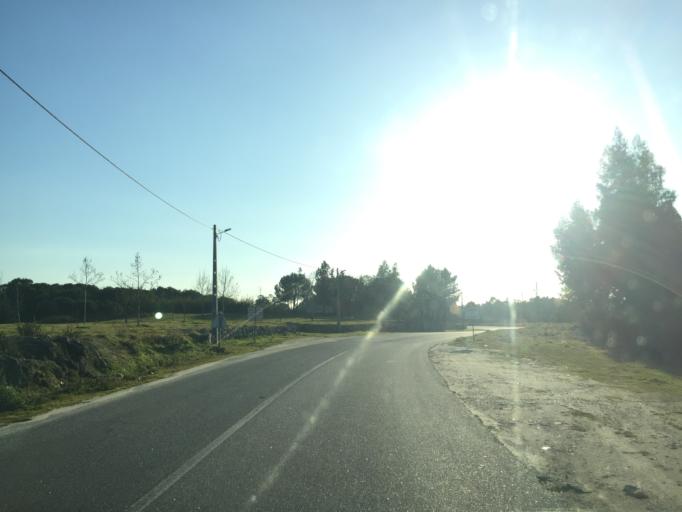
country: PT
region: Viseu
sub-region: Nelas
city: Nelas
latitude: 40.4861
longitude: -7.9101
